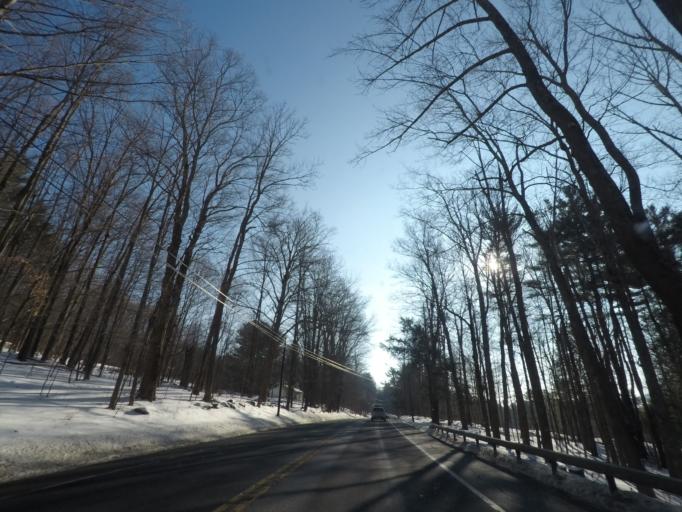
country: US
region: Massachusetts
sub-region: Berkshire County
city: Richmond
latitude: 42.4980
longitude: -73.3700
